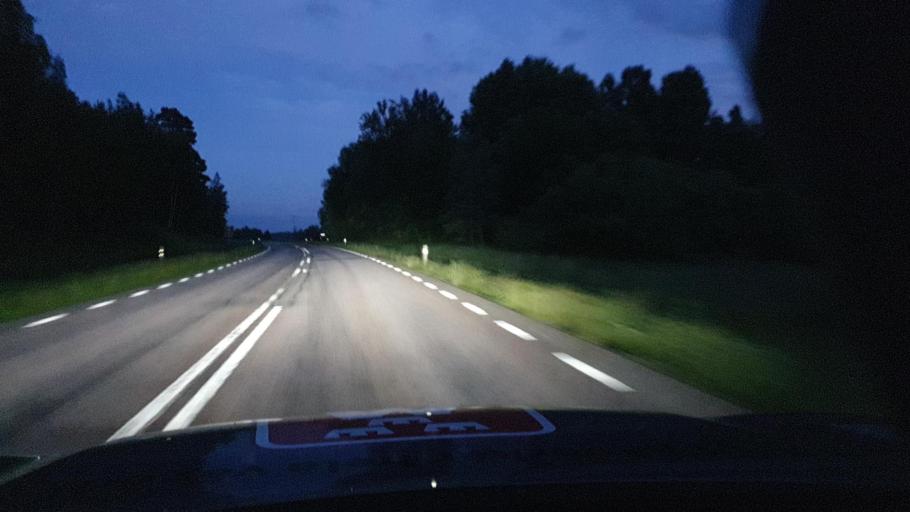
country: SE
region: OErebro
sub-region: Karlskoga Kommun
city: Karlskoga
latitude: 59.4007
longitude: 14.4337
